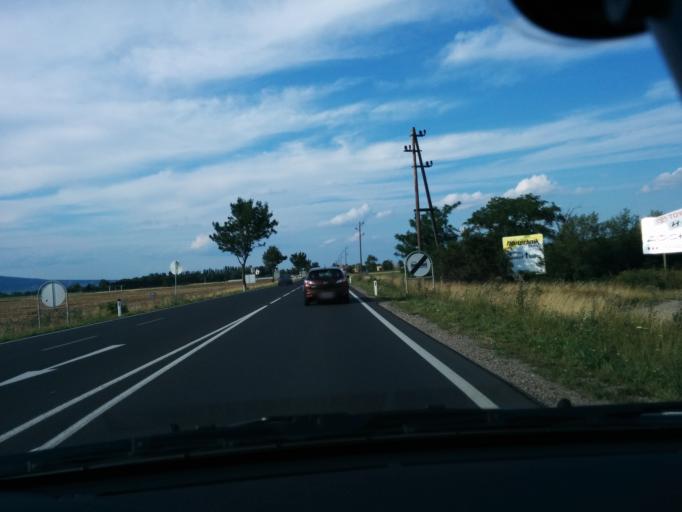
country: AT
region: Lower Austria
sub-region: Politischer Bezirk Baden
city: Gunselsdorf
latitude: 47.9566
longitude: 16.2684
